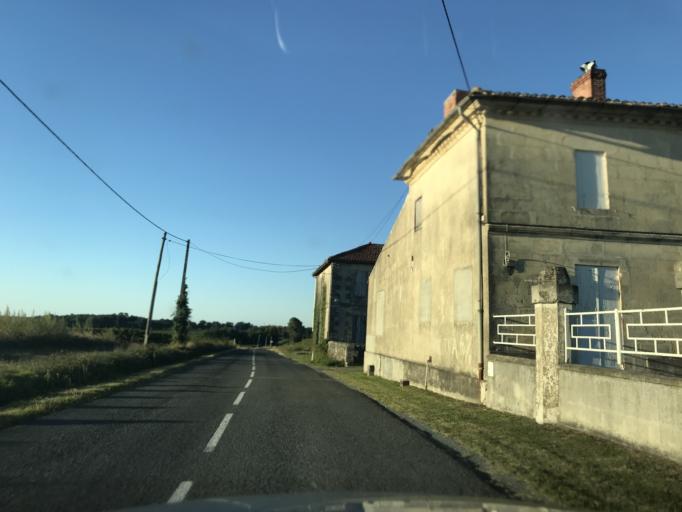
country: FR
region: Aquitaine
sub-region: Departement de la Gironde
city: Lussac
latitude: 44.9570
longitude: -0.0717
